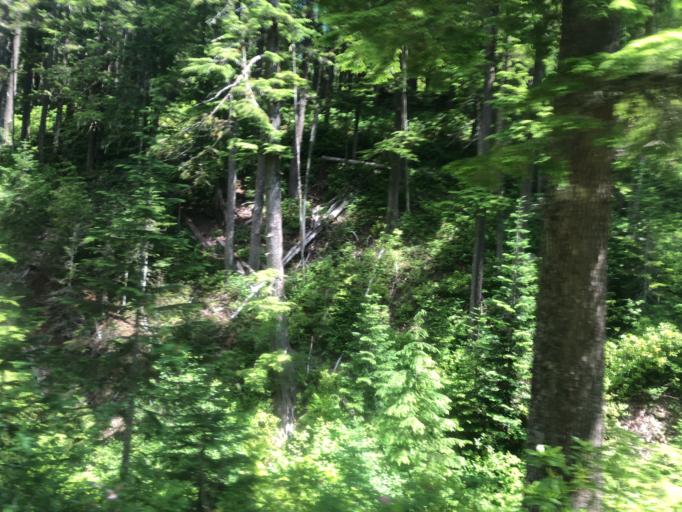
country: US
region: Oregon
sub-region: Clackamas County
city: Mount Hood Village
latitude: 45.4622
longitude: -121.8480
